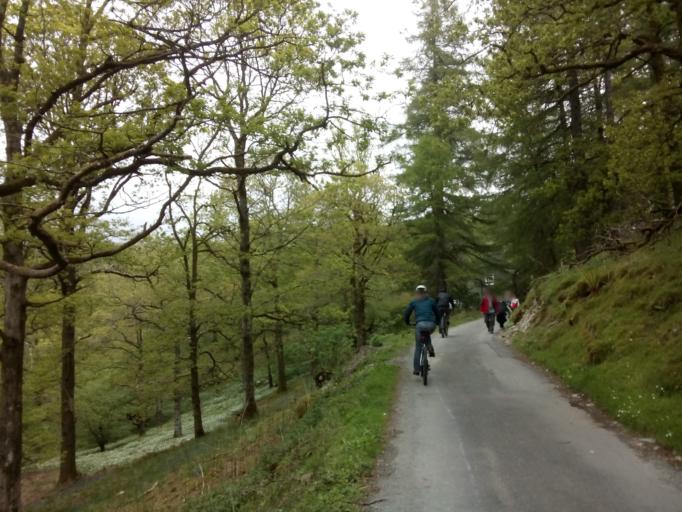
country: GB
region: England
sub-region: Cumbria
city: Ambleside
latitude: 54.4316
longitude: -3.0494
